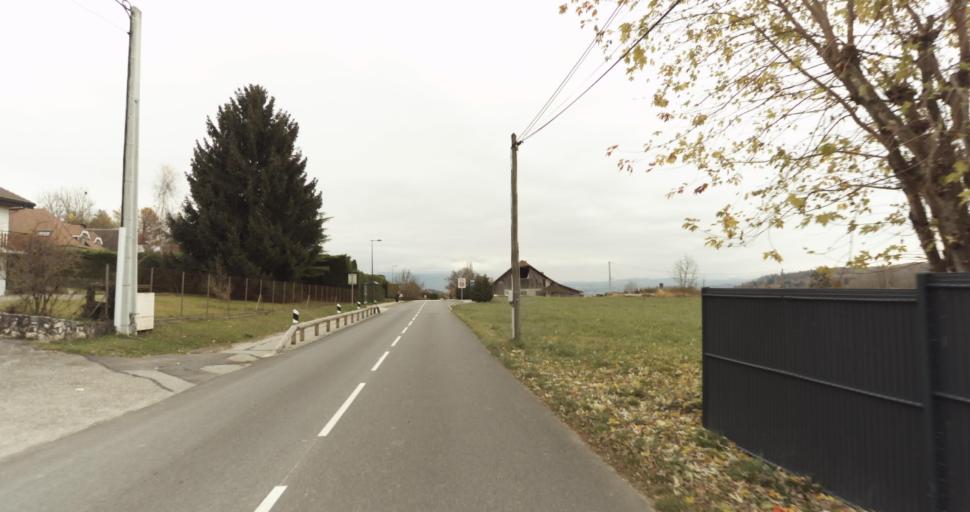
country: FR
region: Rhone-Alpes
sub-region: Departement de la Haute-Savoie
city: Saint-Martin-Bellevue
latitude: 45.9720
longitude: 6.1343
